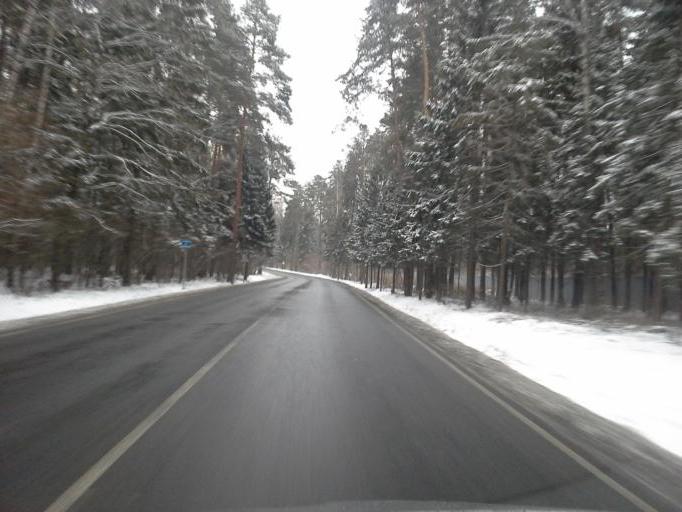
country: RU
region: Moskovskaya
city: Zhavoronki
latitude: 55.7049
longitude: 37.1002
